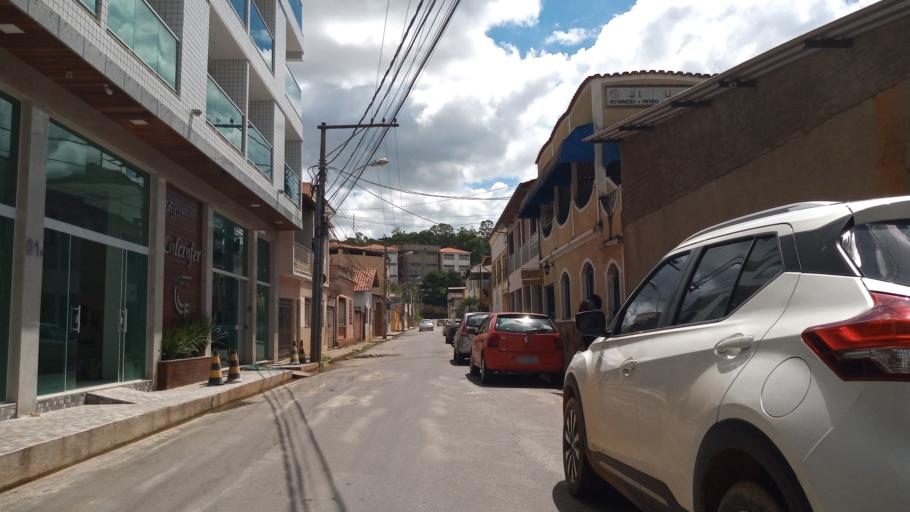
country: BR
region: Minas Gerais
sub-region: Sao Joao Del Rei
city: Sao Joao del Rei
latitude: -21.1232
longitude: -44.2476
